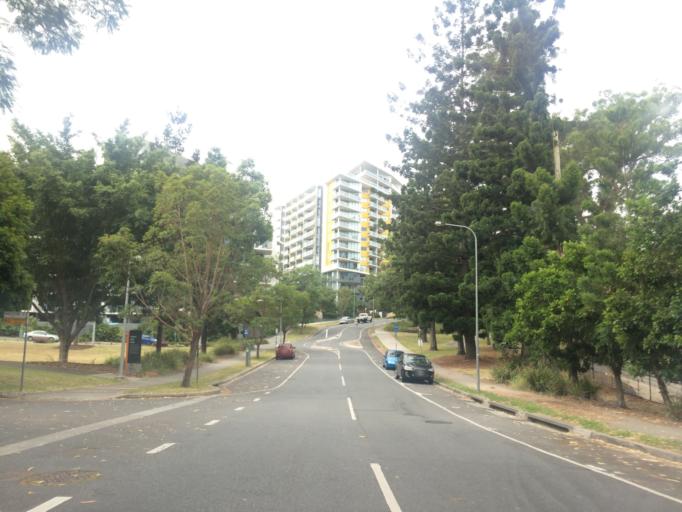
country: AU
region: Queensland
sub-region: Brisbane
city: Spring Hill
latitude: -27.4550
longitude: 153.0162
